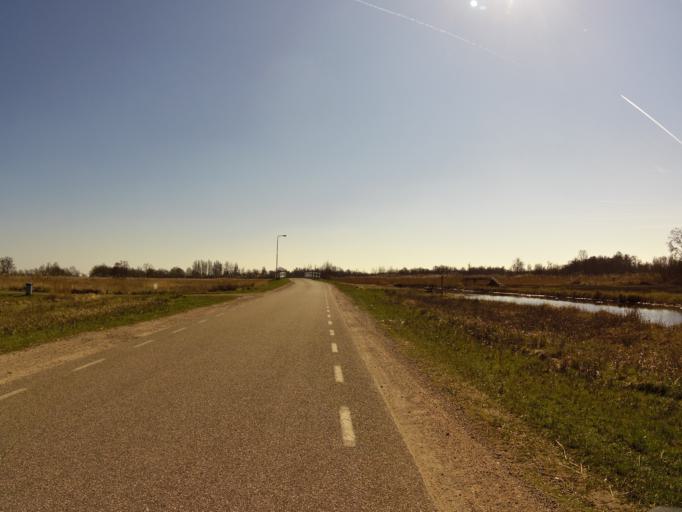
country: NL
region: Overijssel
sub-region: Gemeente Steenwijkerland
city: Oldemarkt
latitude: 52.7859
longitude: 5.9772
